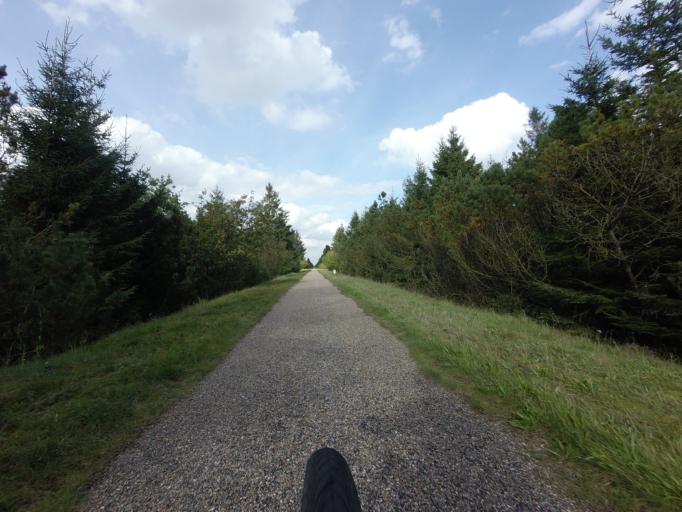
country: DK
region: Central Jutland
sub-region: Viborg Kommune
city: Karup
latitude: 56.2510
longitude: 9.1028
